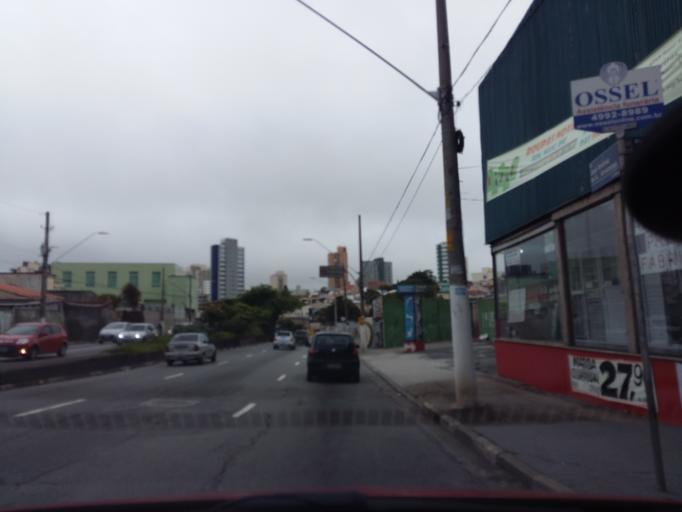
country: BR
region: Sao Paulo
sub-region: Santo Andre
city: Santo Andre
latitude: -23.6605
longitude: -46.5433
